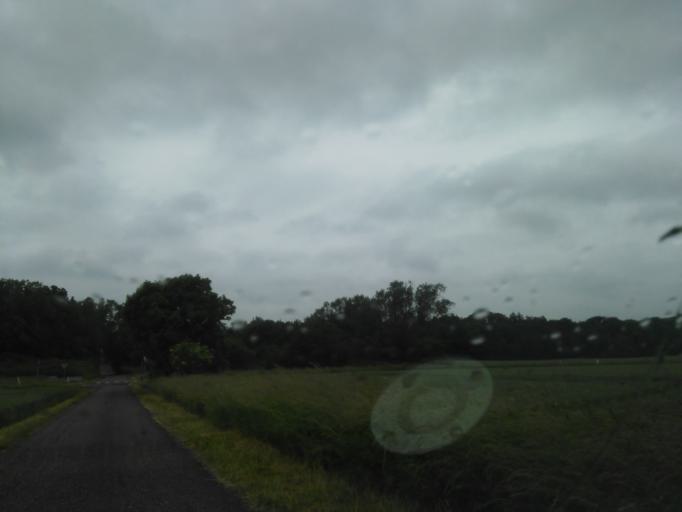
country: DK
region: Capital Region
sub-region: Bornholm Kommune
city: Akirkeby
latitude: 55.0462
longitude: 14.8336
